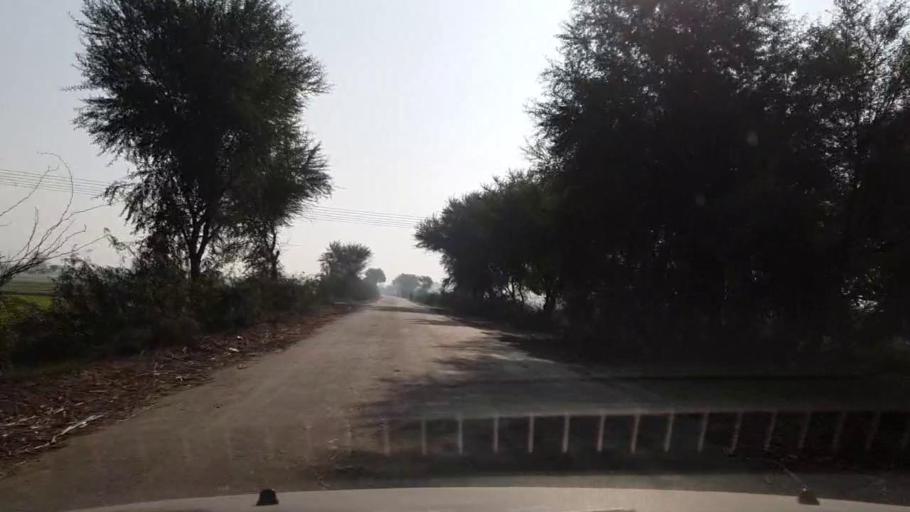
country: PK
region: Sindh
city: Matiari
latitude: 25.5750
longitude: 68.5063
